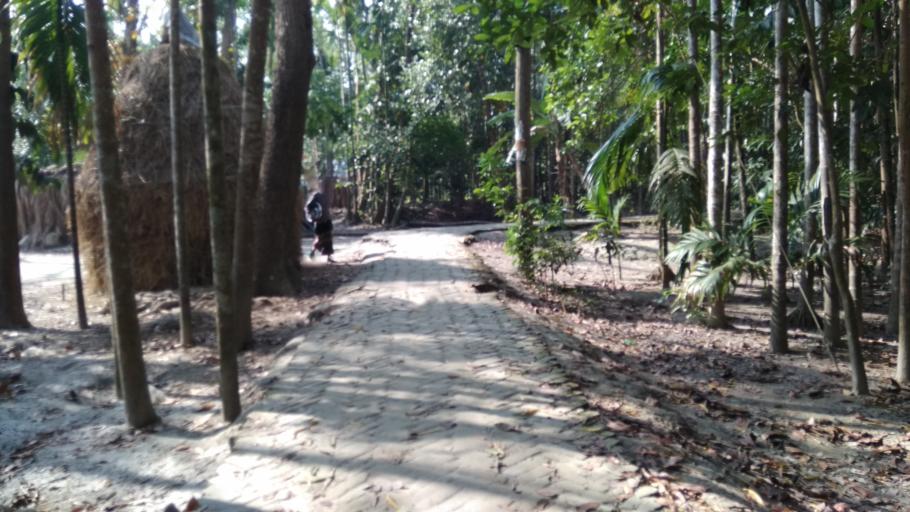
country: BD
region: Barisal
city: Mehendiganj
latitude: 22.9394
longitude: 90.4142
